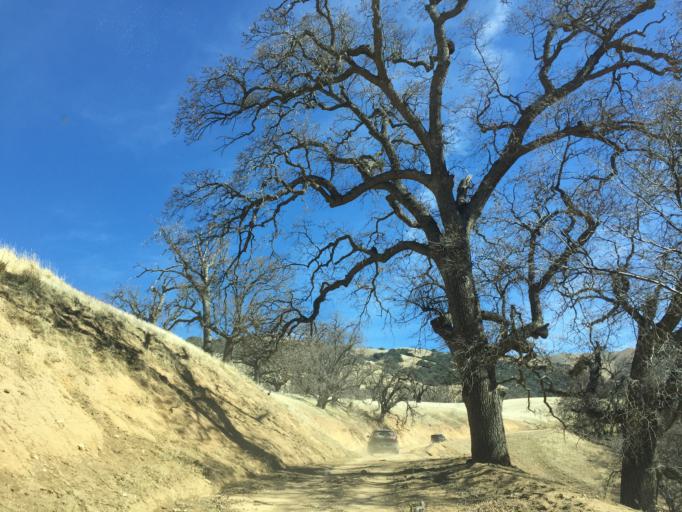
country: US
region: California
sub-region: Kern County
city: Stallion Springs
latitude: 34.9169
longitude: -118.6802
